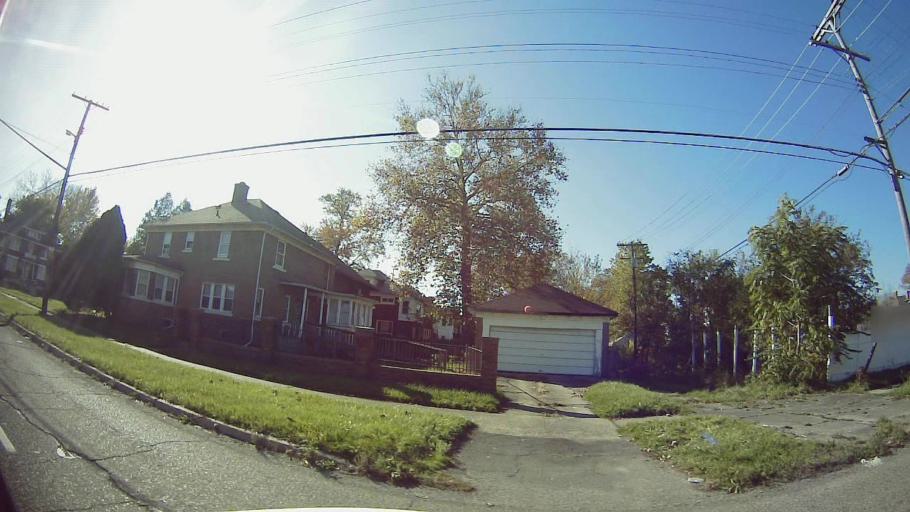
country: US
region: Michigan
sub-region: Wayne County
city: Highland Park
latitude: 42.3812
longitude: -83.1069
